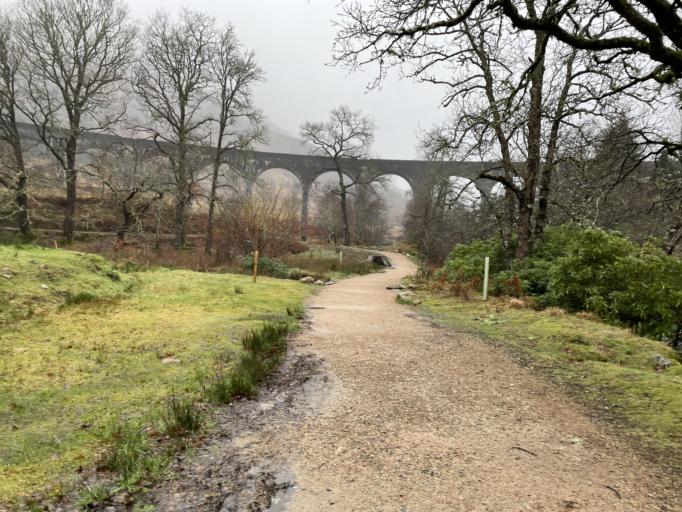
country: GB
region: Scotland
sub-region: Highland
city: Fort William
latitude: 56.8749
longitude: -5.4319
